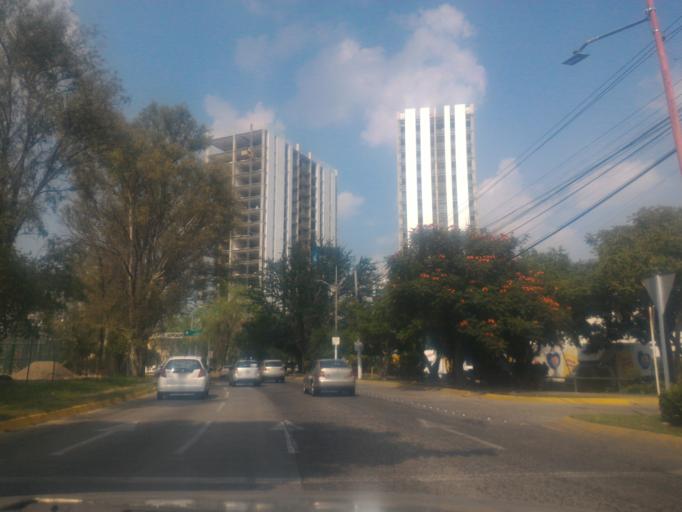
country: MX
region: Jalisco
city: Guadalajara
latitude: 20.6586
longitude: -103.4332
